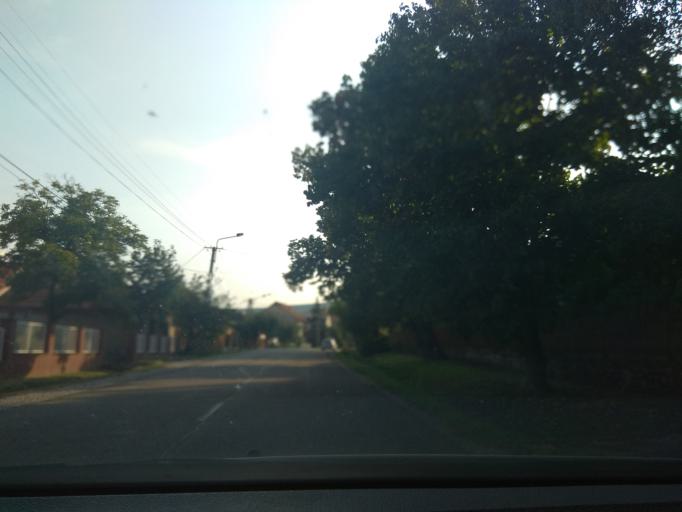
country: HU
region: Heves
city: Felsotarkany
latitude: 47.9762
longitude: 20.4212
